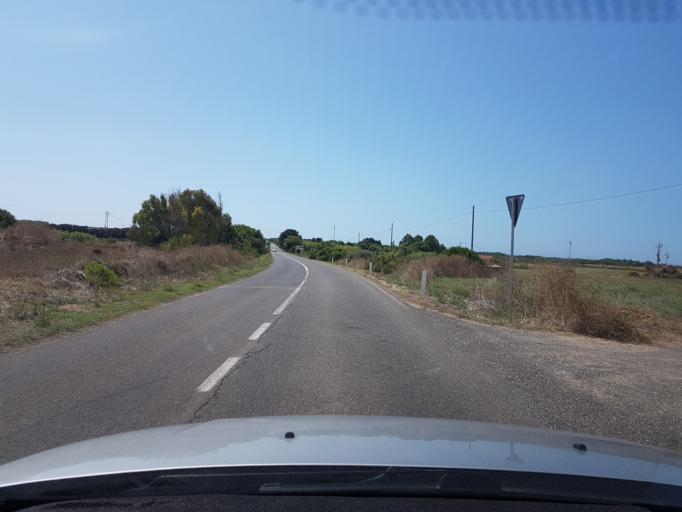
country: IT
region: Sardinia
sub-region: Provincia di Oristano
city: Riola Sardo
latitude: 40.0225
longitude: 8.4748
